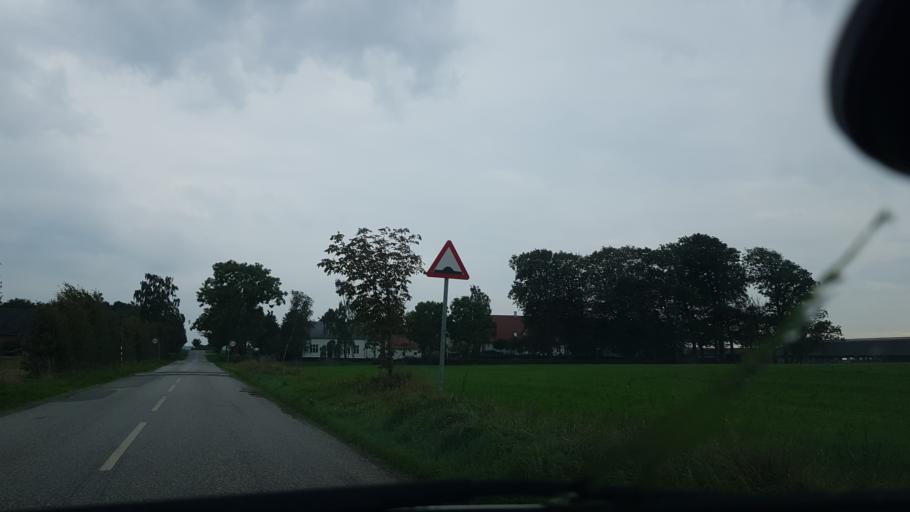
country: DK
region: South Denmark
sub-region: Kolding Kommune
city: Lunderskov
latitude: 55.5340
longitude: 9.3409
